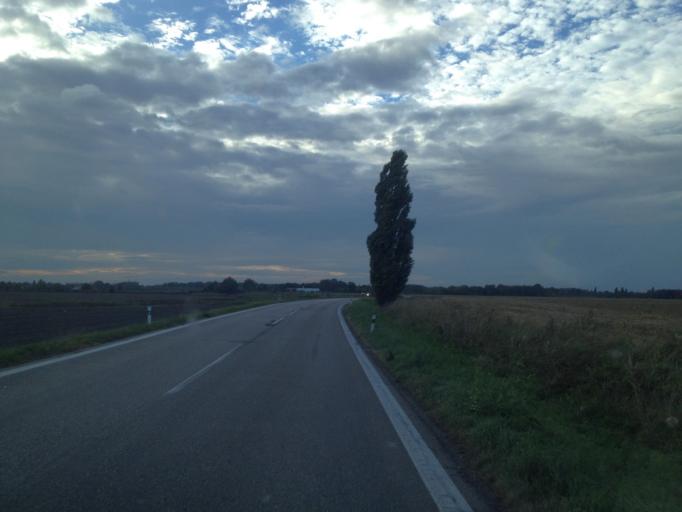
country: SK
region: Nitriansky
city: Komarno
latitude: 47.7635
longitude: 18.1773
